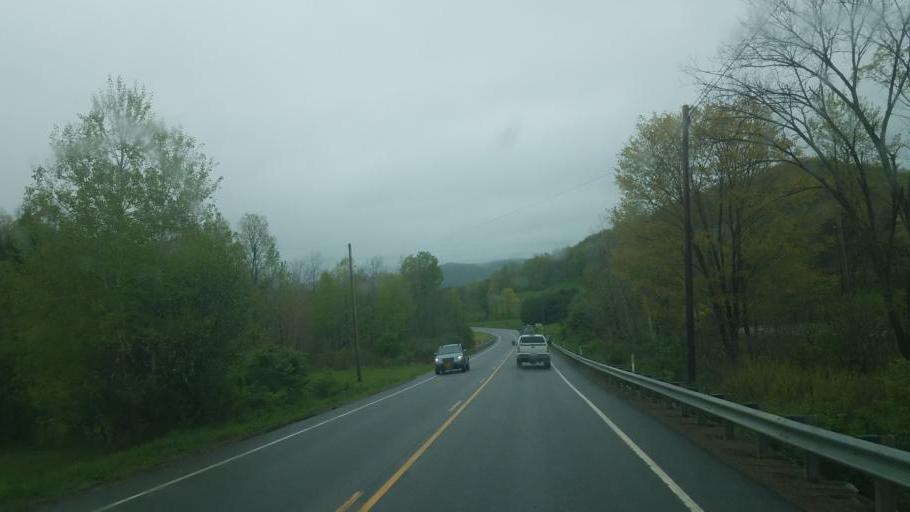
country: US
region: Pennsylvania
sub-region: McKean County
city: Smethport
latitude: 41.8179
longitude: -78.4005
